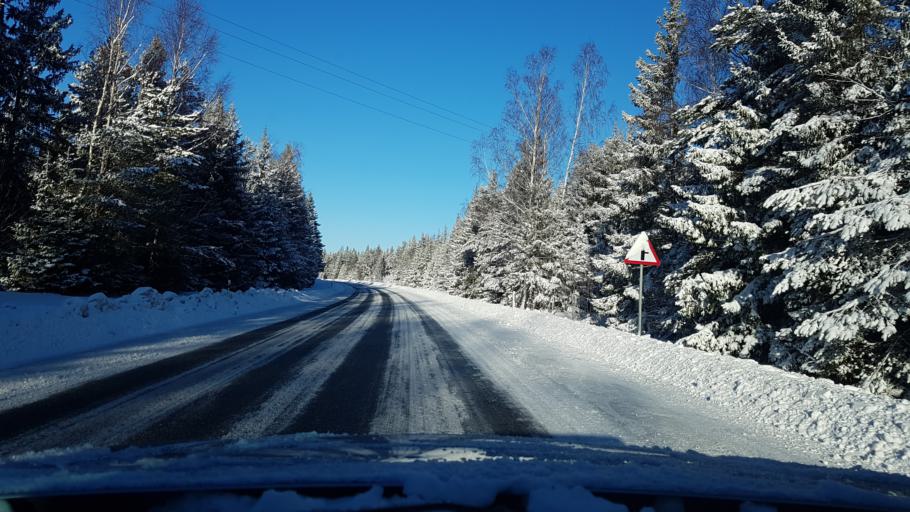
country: EE
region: Hiiumaa
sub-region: Kaerdla linn
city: Kardla
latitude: 58.9800
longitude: 22.8100
